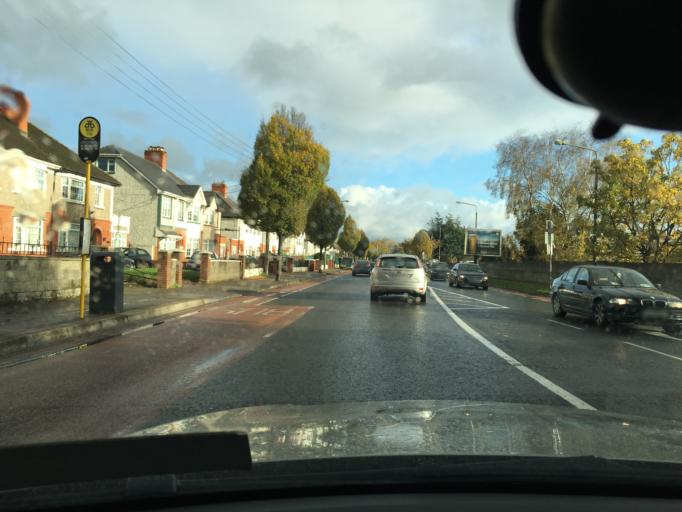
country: IE
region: Leinster
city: Cabra
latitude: 53.3677
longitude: -6.3177
